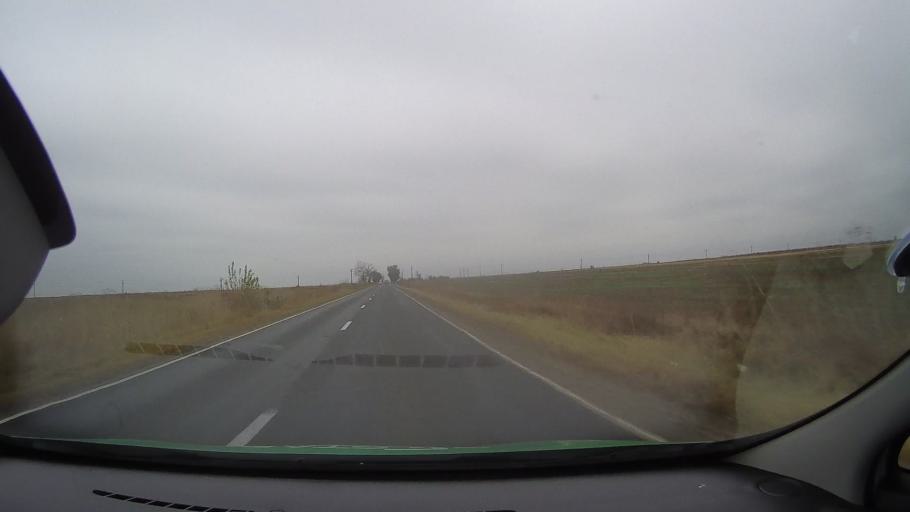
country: RO
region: Ialomita
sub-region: Comuna Scanteia
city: Scanteia
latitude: 44.7694
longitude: 27.4716
